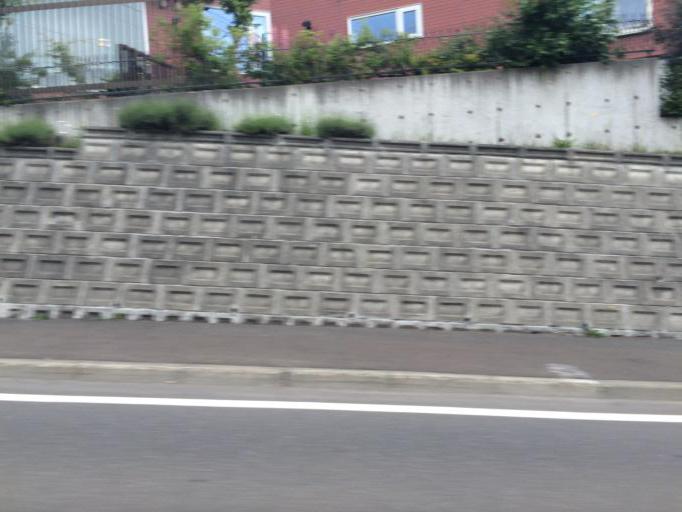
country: JP
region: Hokkaido
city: Sapporo
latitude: 43.0417
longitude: 141.2907
